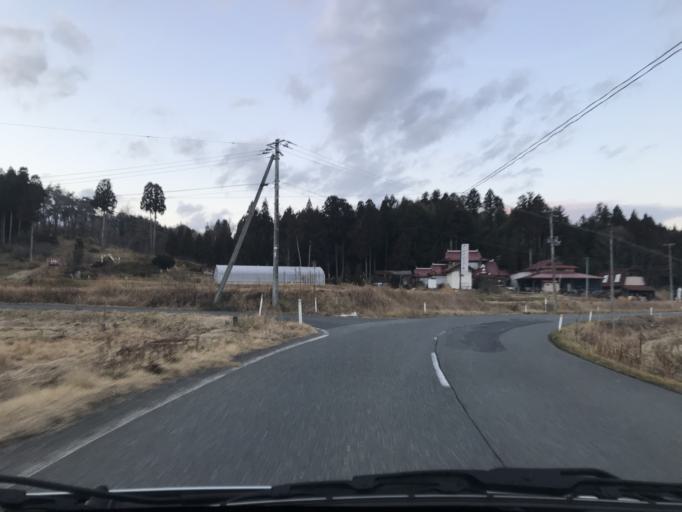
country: JP
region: Iwate
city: Ichinoseki
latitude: 38.8254
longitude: 141.1177
